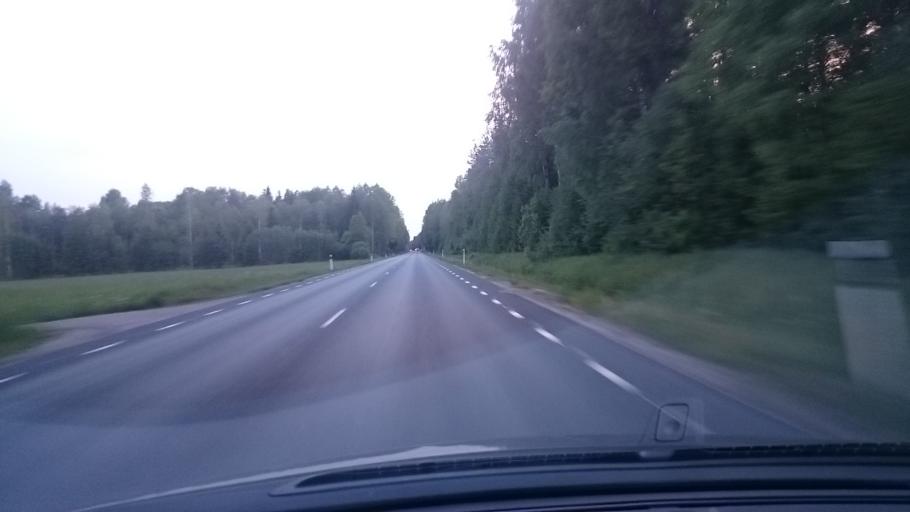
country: EE
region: Paernumaa
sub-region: Vaendra vald (alev)
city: Vandra
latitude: 58.8416
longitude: 25.0616
